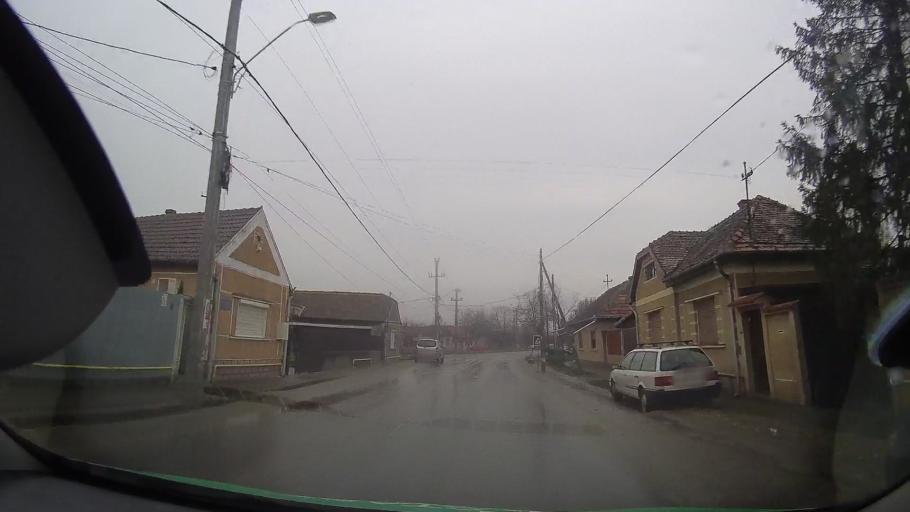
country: RO
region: Bihor
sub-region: Municipiul Salonta
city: Salonta
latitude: 46.7973
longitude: 21.6551
